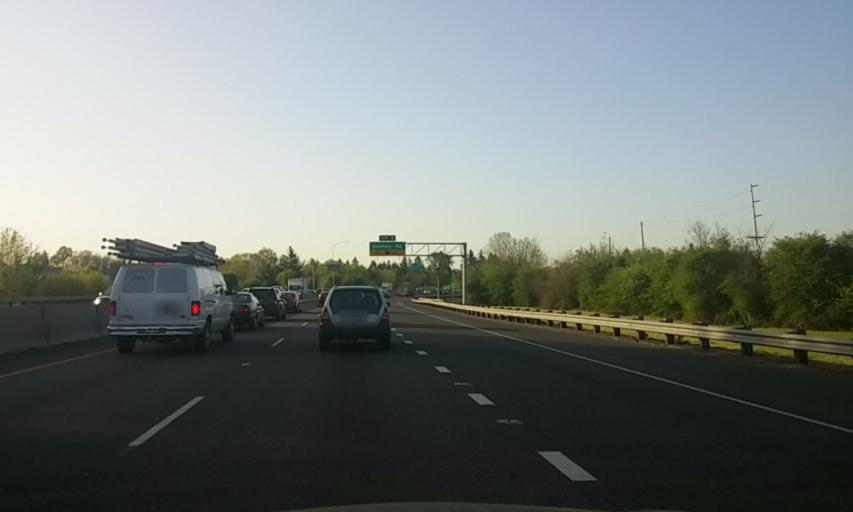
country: US
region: Oregon
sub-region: Washington County
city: Beaverton
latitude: 45.4741
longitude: -122.7877
